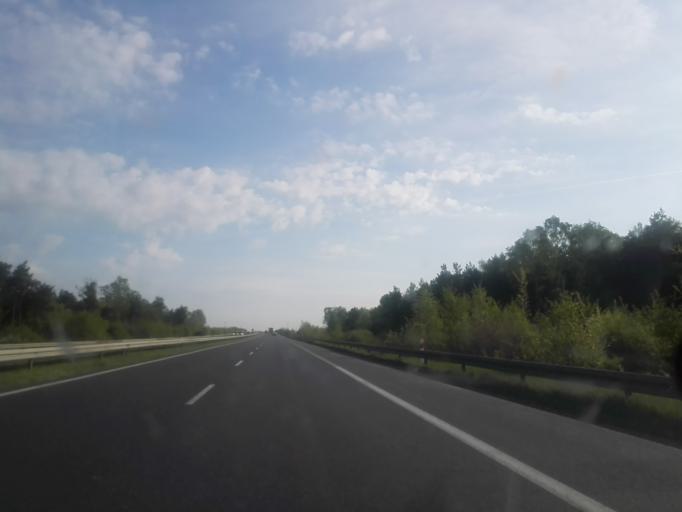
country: PL
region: Lodz Voivodeship
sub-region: Powiat piotrkowski
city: Wola Krzysztoporska
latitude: 51.3477
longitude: 19.6017
